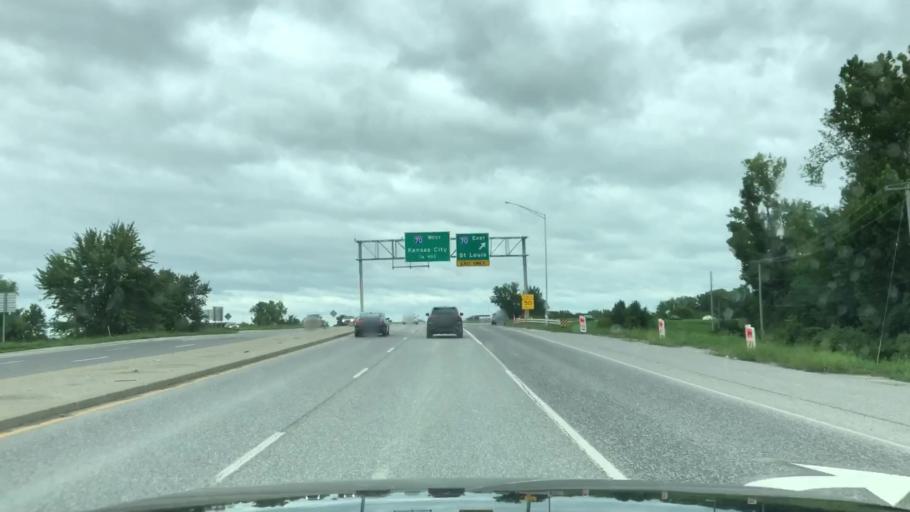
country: US
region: Missouri
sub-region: Saint Charles County
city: Saint Charles
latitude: 38.7515
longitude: -90.4611
